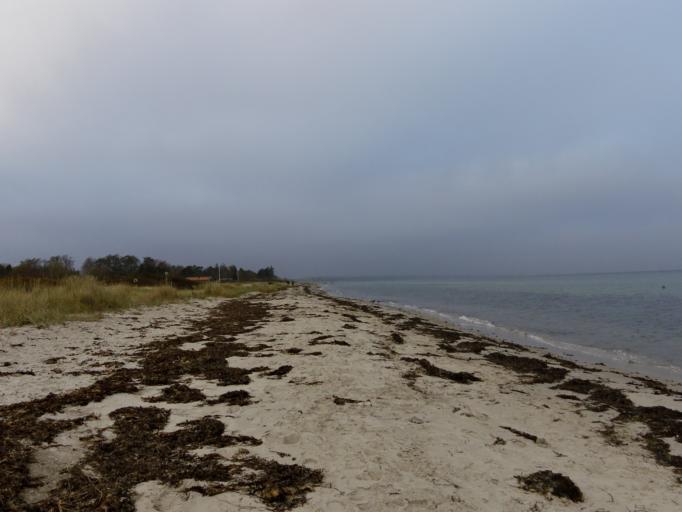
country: DK
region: Central Jutland
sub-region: Arhus Kommune
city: Malling
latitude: 55.9632
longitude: 10.2639
